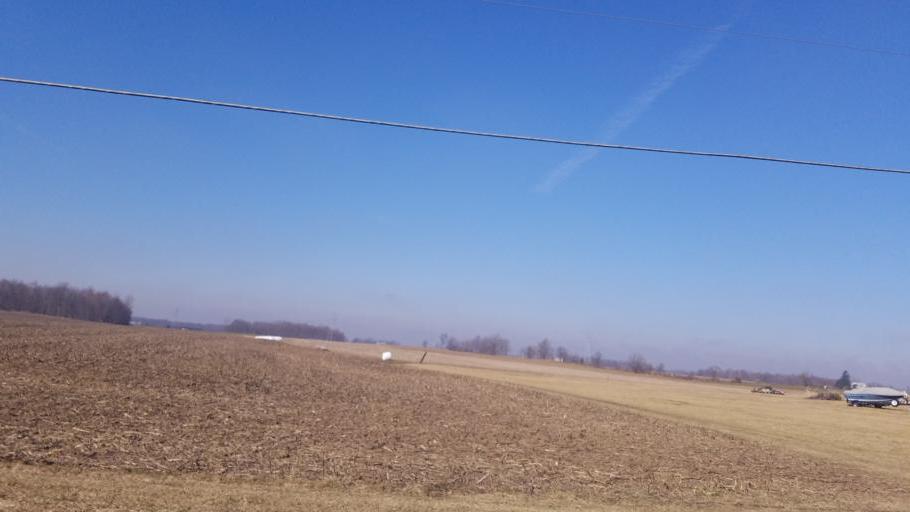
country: US
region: Ohio
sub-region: Crawford County
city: Bucyrus
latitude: 40.8394
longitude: -82.9701
